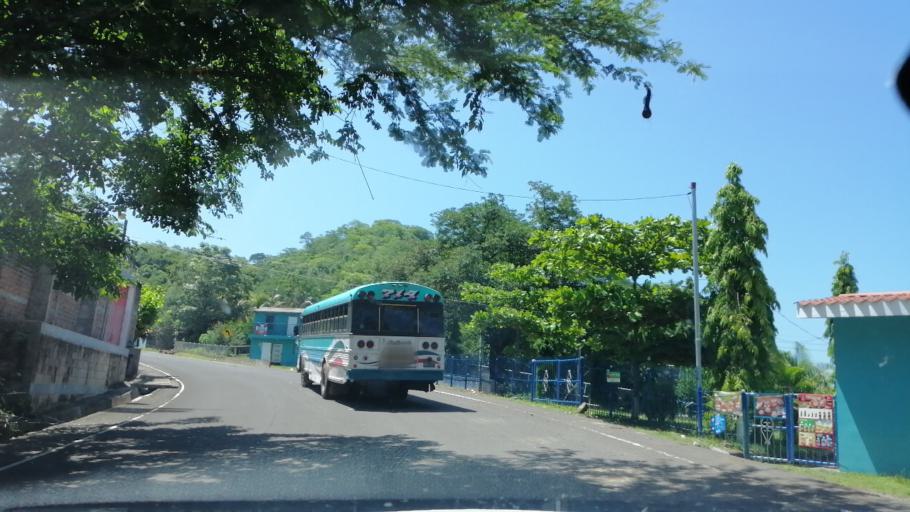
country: SV
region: San Miguel
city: Sesori
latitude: 13.8050
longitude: -88.3964
